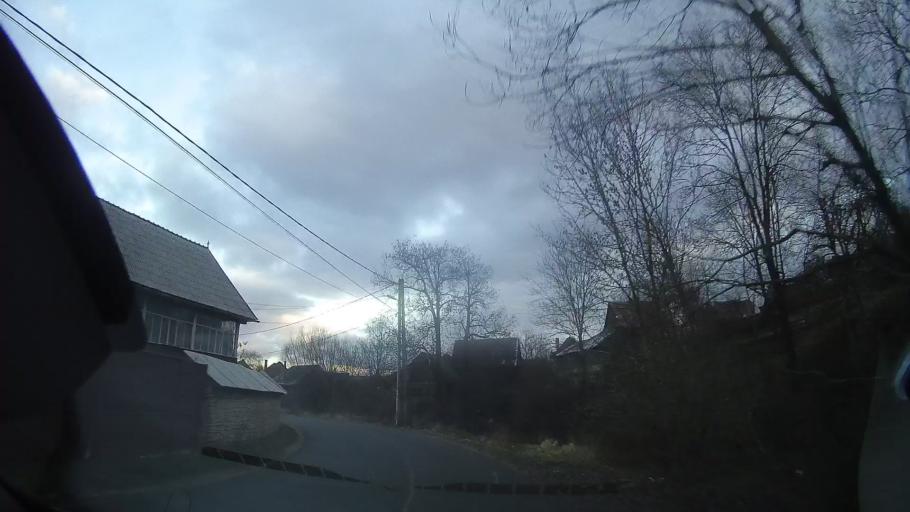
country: RO
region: Cluj
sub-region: Comuna Manastireni
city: Manastireni
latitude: 46.7810
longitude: 23.0761
